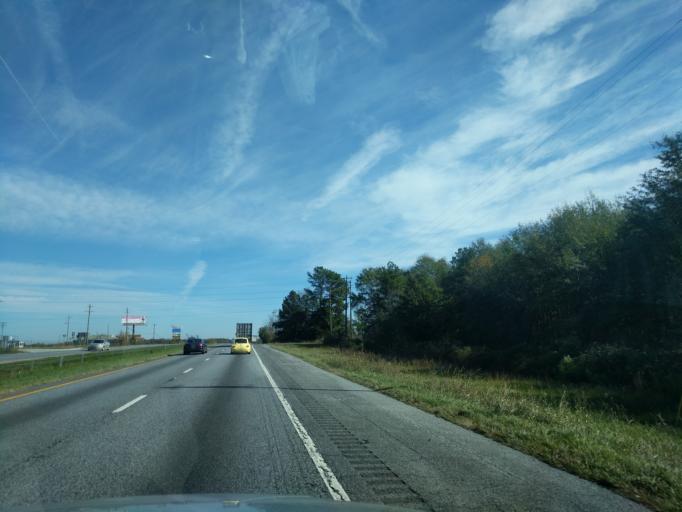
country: US
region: South Carolina
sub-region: Spartanburg County
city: Cowpens
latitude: 35.0440
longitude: -81.8165
